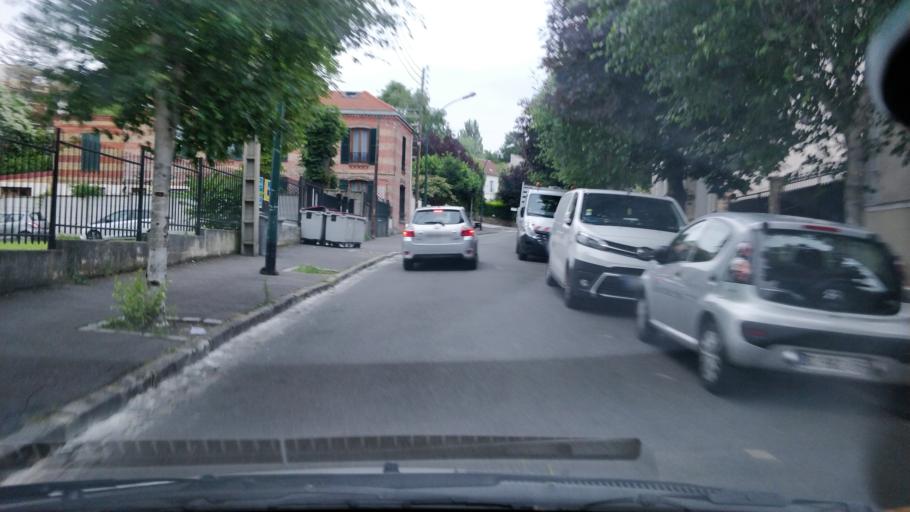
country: FR
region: Ile-de-France
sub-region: Departement de Seine-Saint-Denis
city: Le Raincy
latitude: 48.9003
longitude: 2.5236
